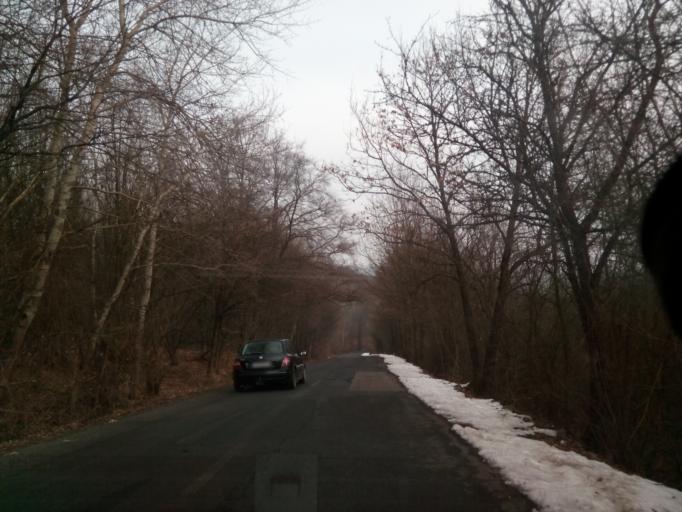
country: HU
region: Borsod-Abauj-Zemplen
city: Gonc
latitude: 48.4855
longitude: 21.3959
